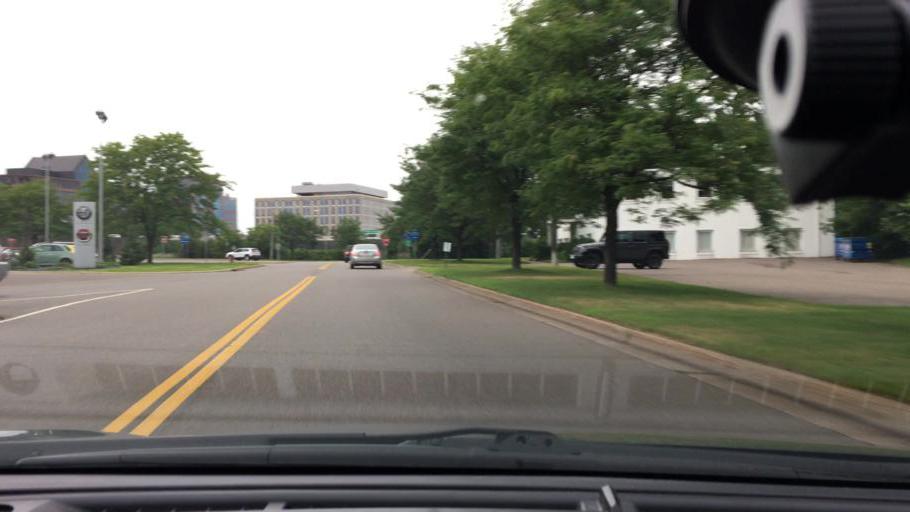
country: US
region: Minnesota
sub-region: Hennepin County
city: Saint Louis Park
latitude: 44.9632
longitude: -93.3420
